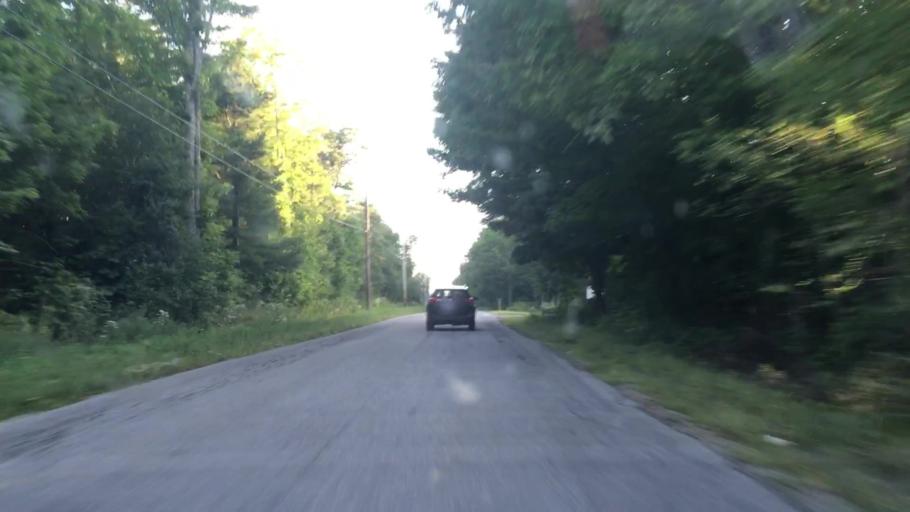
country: US
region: Maine
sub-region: Waldo County
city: Frankfort
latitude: 44.6805
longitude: -68.9135
